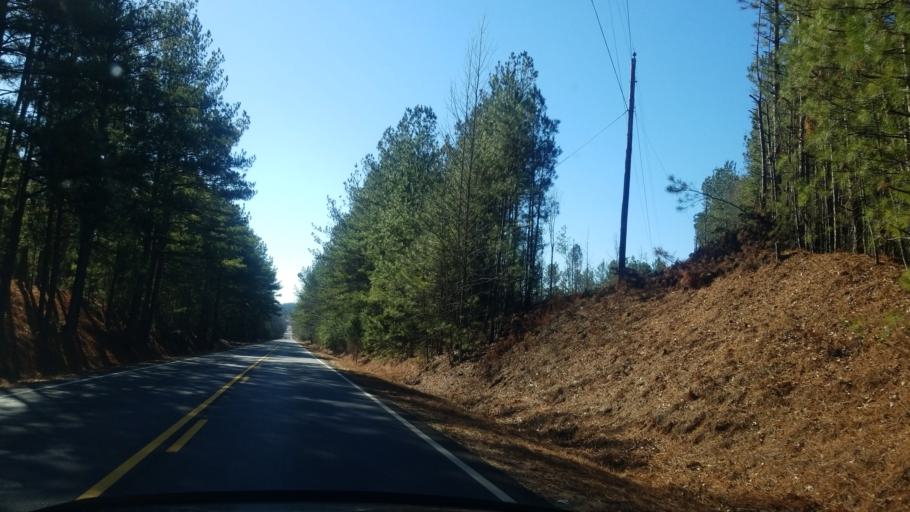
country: US
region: Alabama
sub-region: Chambers County
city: Valley
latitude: 32.8036
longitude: -85.1030
